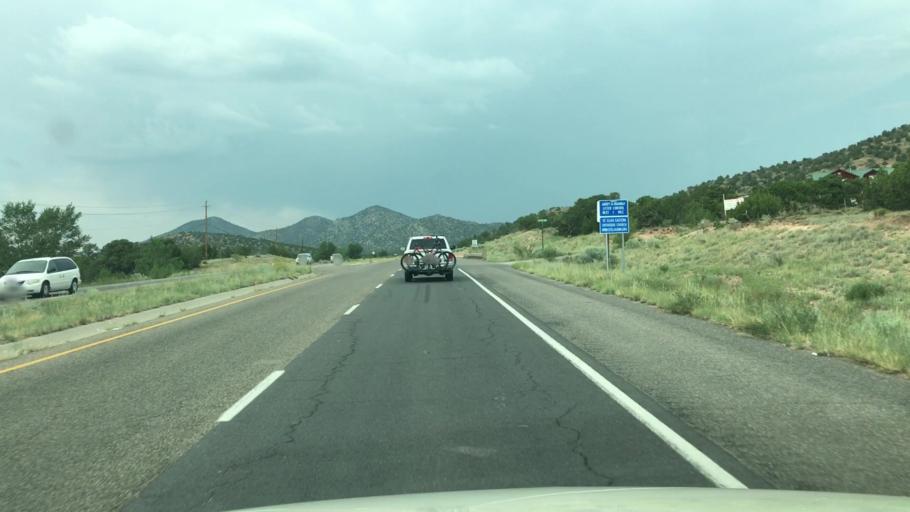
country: US
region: New Mexico
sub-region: Santa Fe County
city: Eldorado at Santa Fe
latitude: 35.5405
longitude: -105.8854
